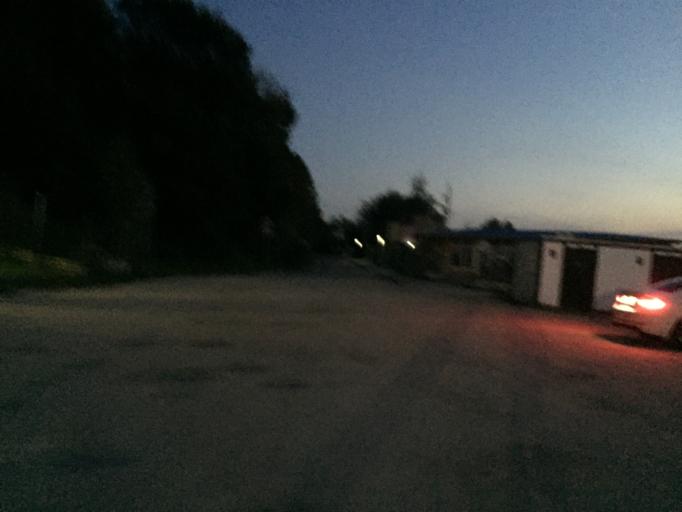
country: RU
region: Kaliningrad
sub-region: Gorod Kaliningrad
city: Yantarnyy
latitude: 54.8836
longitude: 19.9348
